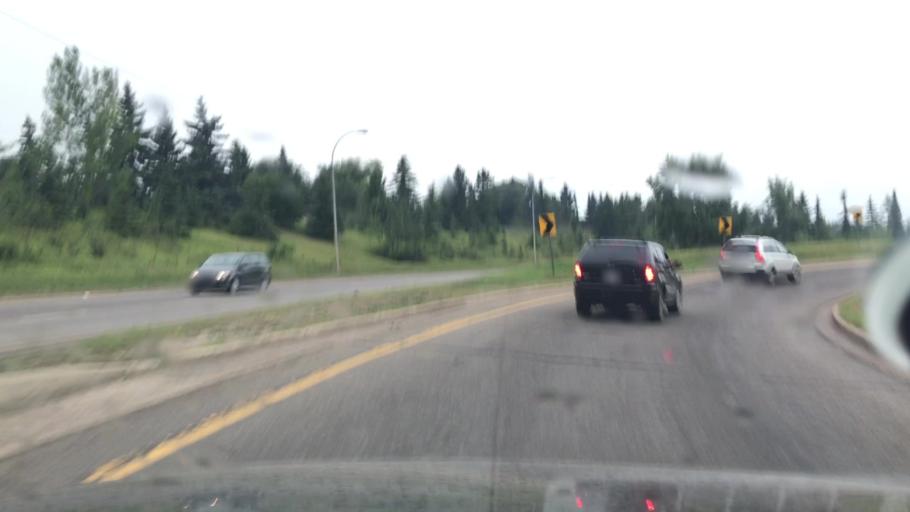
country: CA
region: Alberta
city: Edmonton
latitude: 53.4833
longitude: -113.5720
